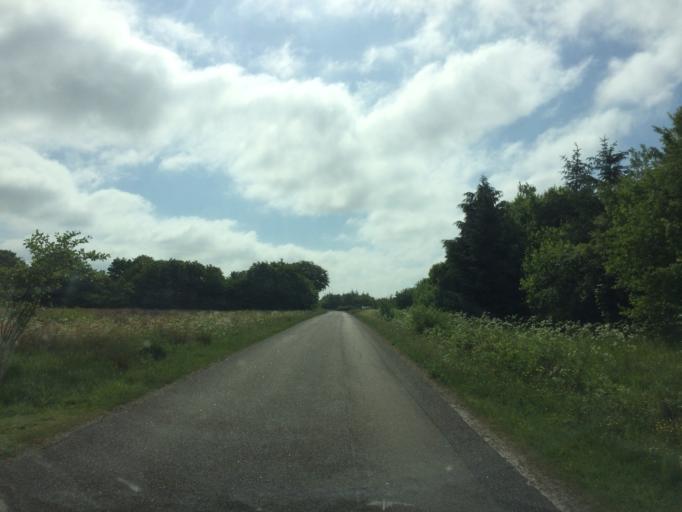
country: DK
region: Central Jutland
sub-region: Holstebro Kommune
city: Ulfborg
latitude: 56.2224
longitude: 8.4392
